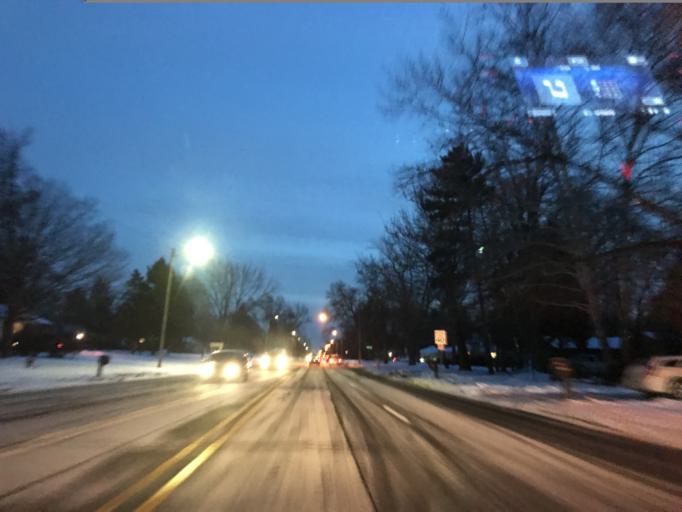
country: US
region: Michigan
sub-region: Wayne County
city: Redford
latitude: 42.4125
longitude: -83.3156
